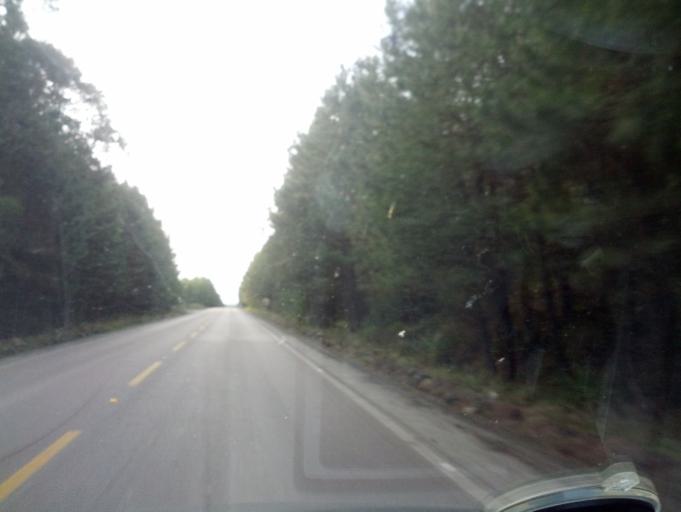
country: BR
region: Santa Catarina
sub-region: Otacilio Costa
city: Otacilio Costa
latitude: -27.3765
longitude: -50.1345
